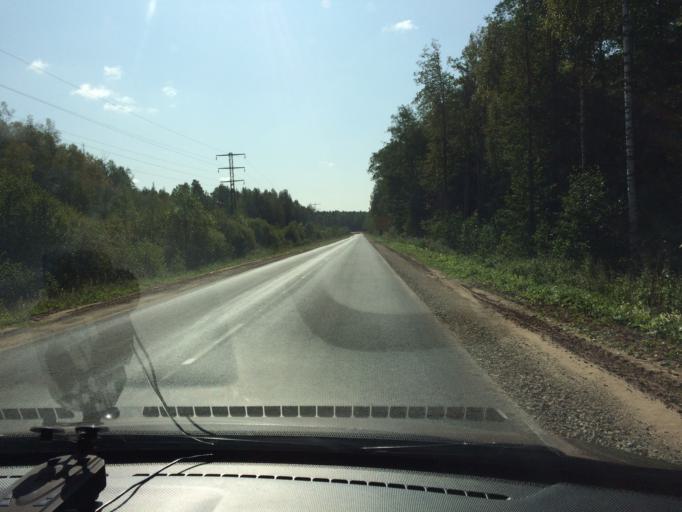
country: RU
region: Mariy-El
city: Surok
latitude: 56.5553
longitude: 48.3117
